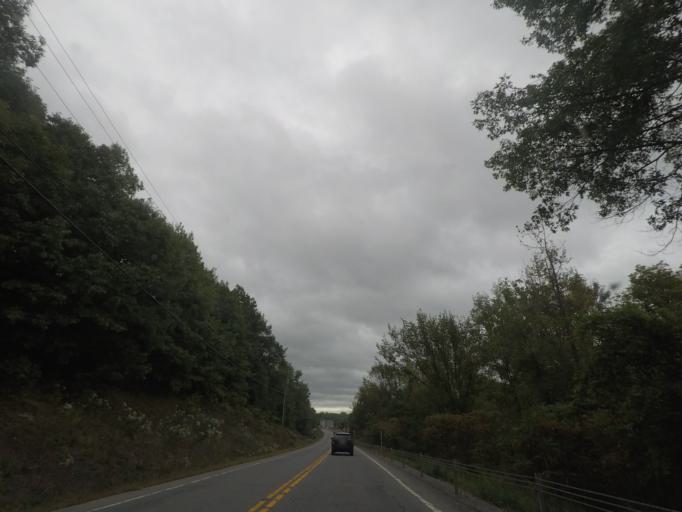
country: US
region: New York
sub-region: Saratoga County
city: Mechanicville
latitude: 42.9129
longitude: -73.7009
